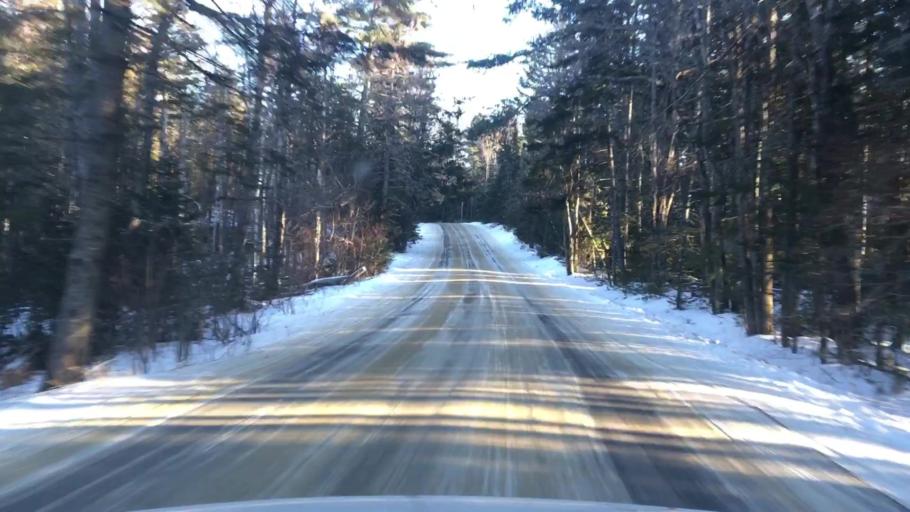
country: US
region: Maine
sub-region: Hancock County
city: Castine
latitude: 44.3833
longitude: -68.7335
